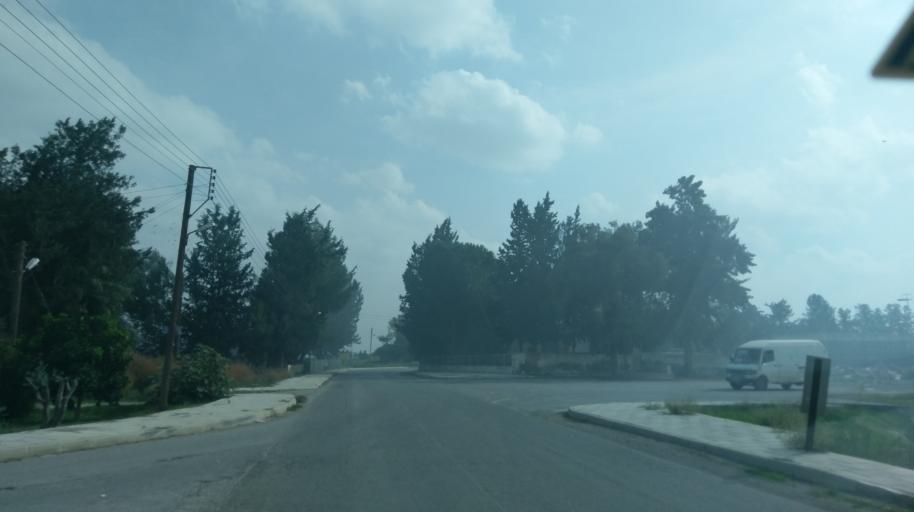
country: CY
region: Lefkosia
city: Mammari
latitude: 35.2309
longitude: 33.1676
